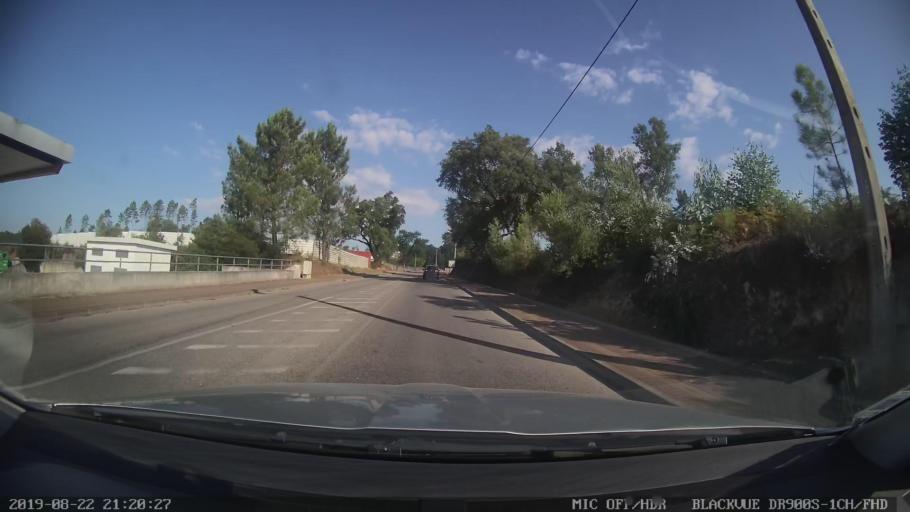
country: PT
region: Castelo Branco
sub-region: Serta
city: Serta
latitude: 39.8126
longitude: -8.1078
